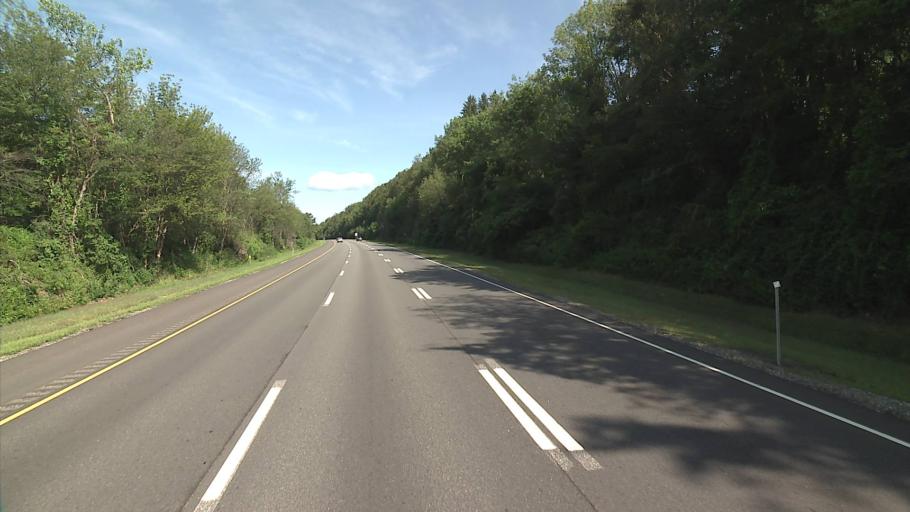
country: US
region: Connecticut
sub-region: Hartford County
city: Terramuggus
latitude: 41.6404
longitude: -72.4623
